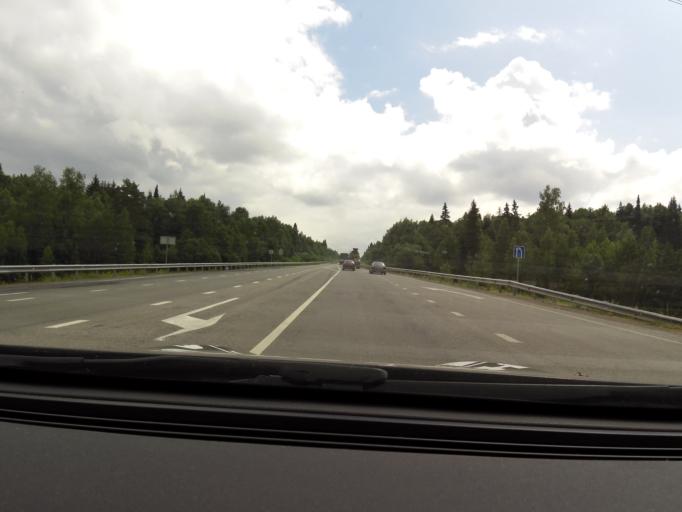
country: RU
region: Perm
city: Kungur
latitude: 57.3268
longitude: 56.9582
